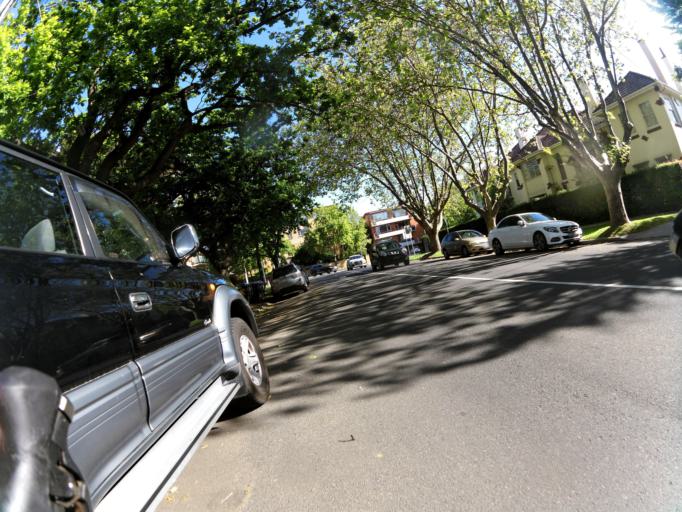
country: AU
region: Victoria
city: Toorak
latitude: -37.8416
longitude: 145.0185
